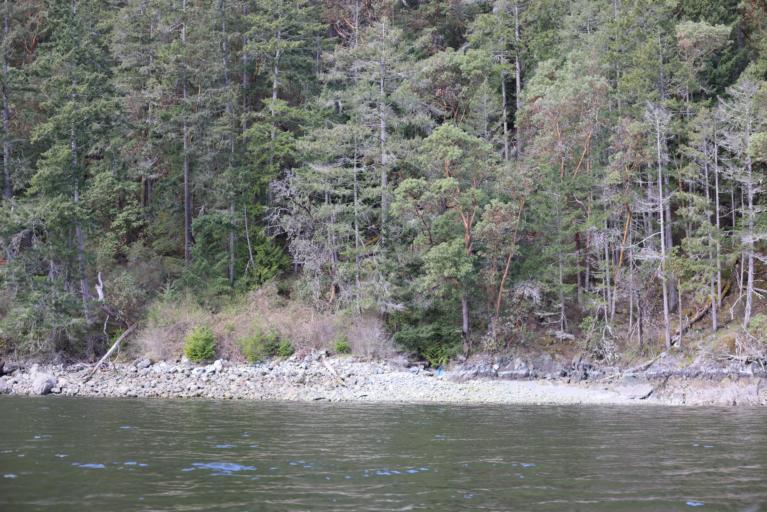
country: CA
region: British Columbia
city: Langford
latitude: 48.5446
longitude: -123.5573
